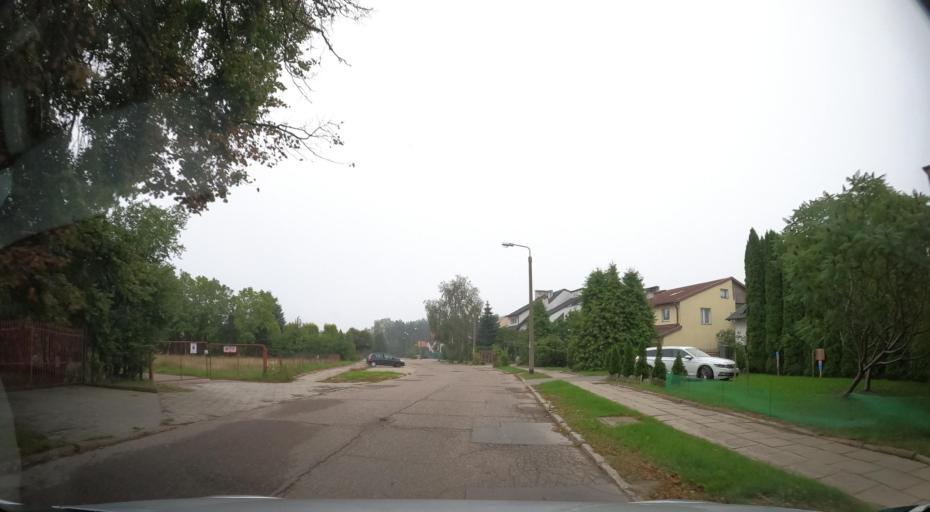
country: PL
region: Pomeranian Voivodeship
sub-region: Powiat kartuski
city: Chwaszczyno
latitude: 54.4250
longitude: 18.4623
